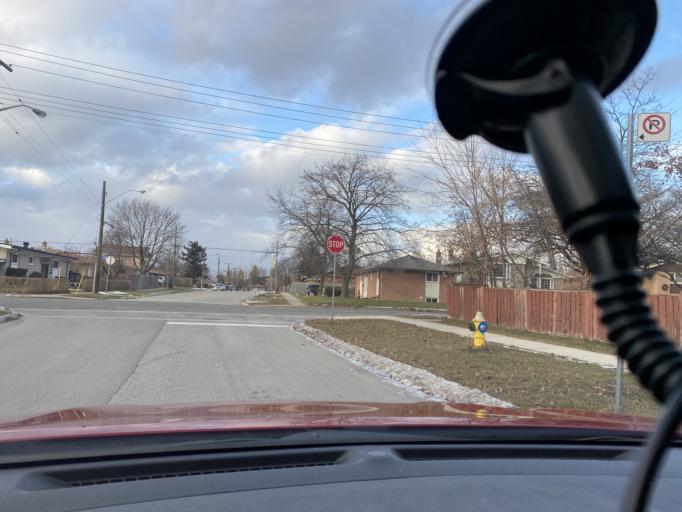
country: CA
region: Ontario
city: Scarborough
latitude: 43.7698
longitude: -79.2174
